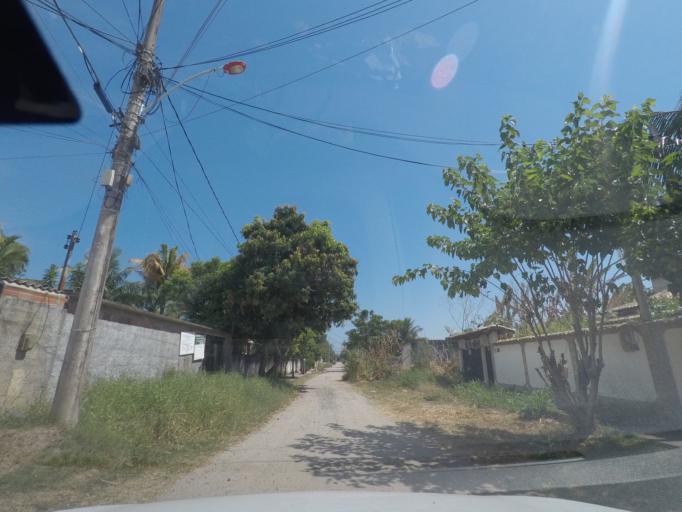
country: BR
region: Rio de Janeiro
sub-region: Marica
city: Marica
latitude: -22.9533
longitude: -42.9630
